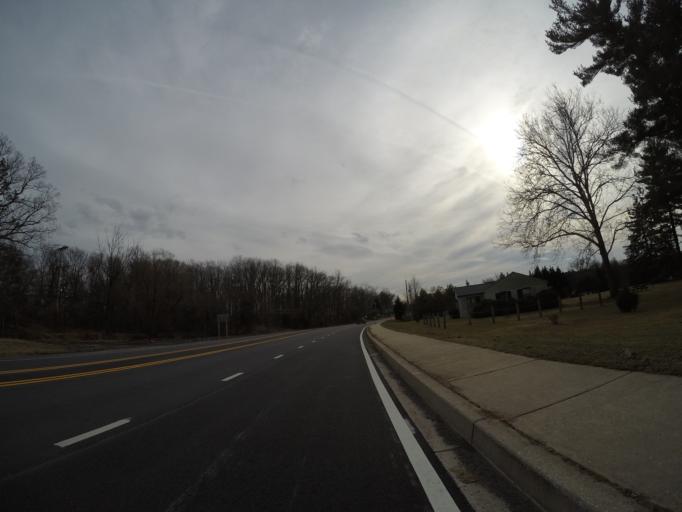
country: US
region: Maryland
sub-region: Howard County
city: Ellicott City
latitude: 39.2354
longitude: -76.7983
